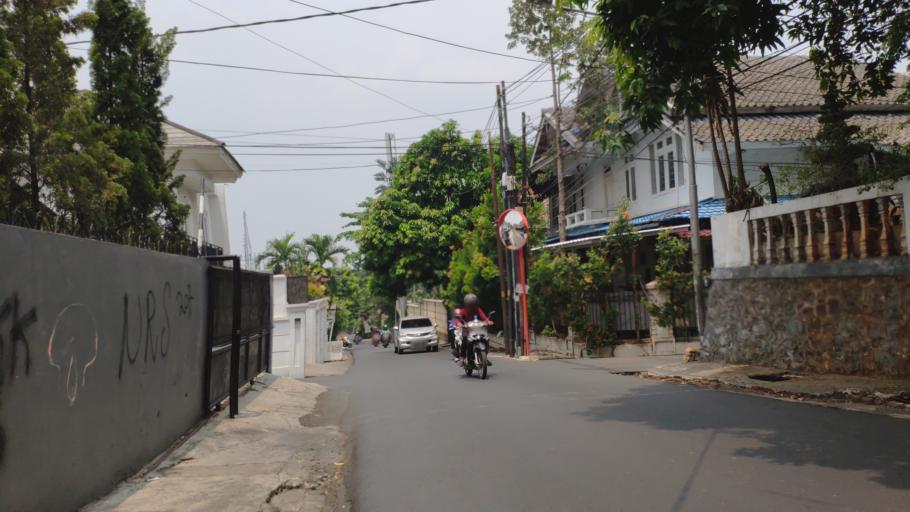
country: ID
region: Banten
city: South Tangerang
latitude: -6.2666
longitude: 106.7720
